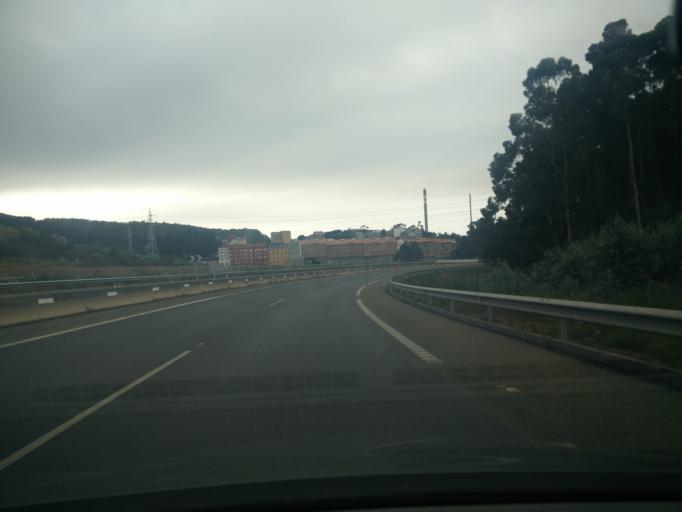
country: ES
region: Galicia
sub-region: Provincia da Coruna
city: Arteixo
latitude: 43.3358
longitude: -8.4550
